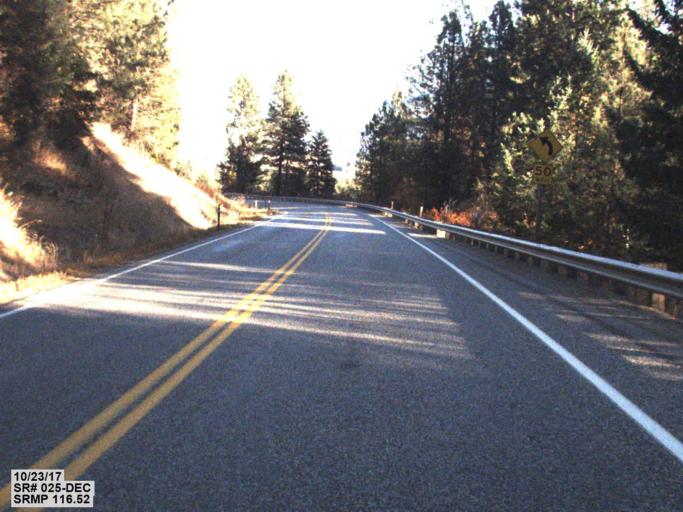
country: CA
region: British Columbia
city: Rossland
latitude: 48.9439
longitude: -117.7882
